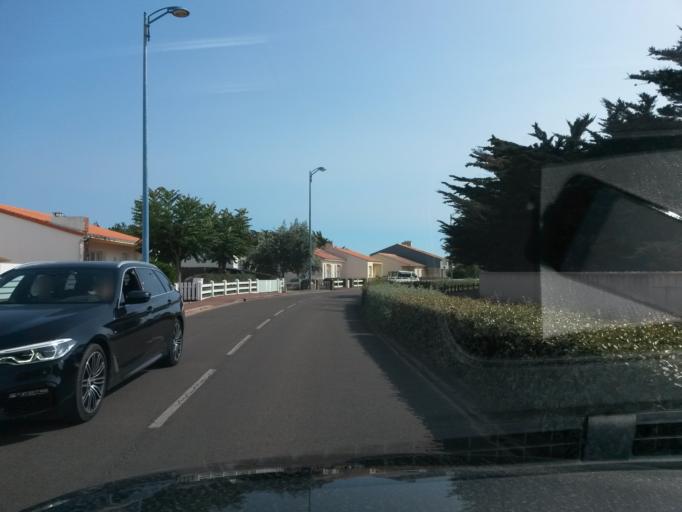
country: FR
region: Pays de la Loire
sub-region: Departement de la Vendee
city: Bretignolles-sur-Mer
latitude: 46.6217
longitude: -1.8723
